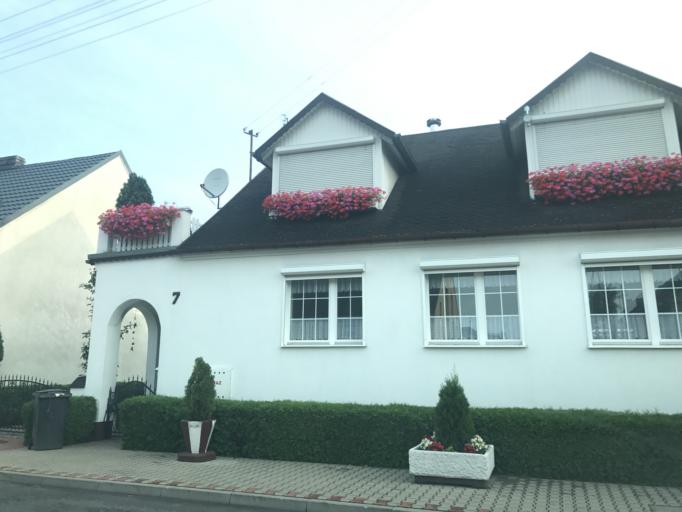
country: PL
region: Greater Poland Voivodeship
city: Miejska Gorka
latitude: 51.6552
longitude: 16.9621
